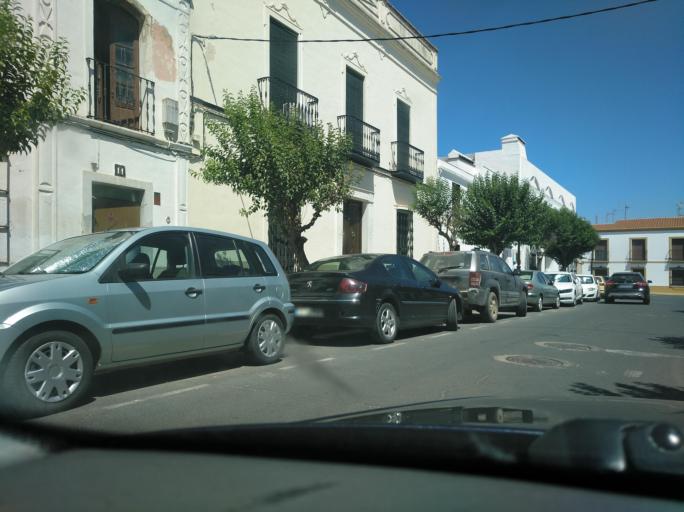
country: ES
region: Extremadura
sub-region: Provincia de Badajoz
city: Olivenza
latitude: 38.6856
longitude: -7.1023
